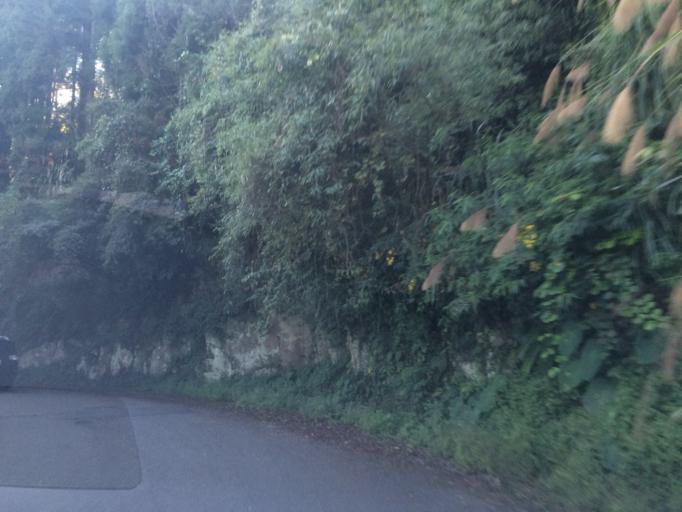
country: TW
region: Taiwan
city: Lugu
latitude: 23.6568
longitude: 120.7795
